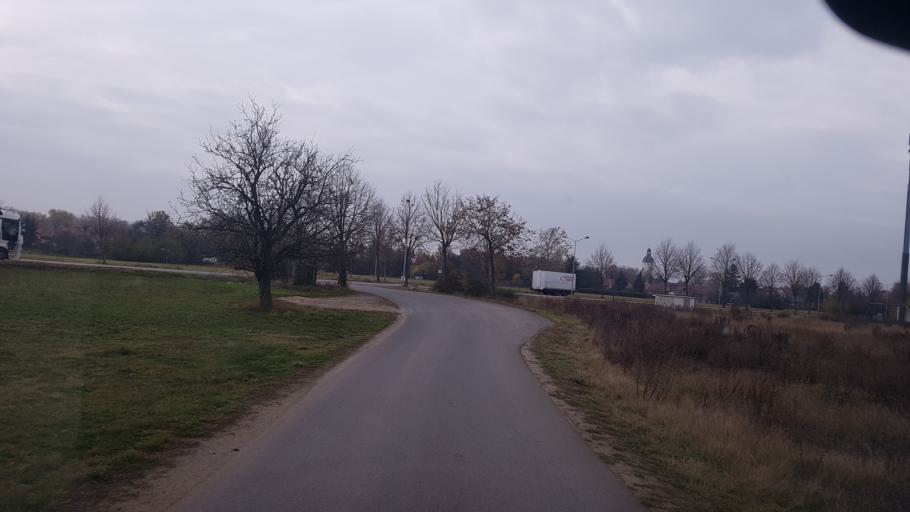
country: DE
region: Brandenburg
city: Falkenberg
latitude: 51.5993
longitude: 13.3007
